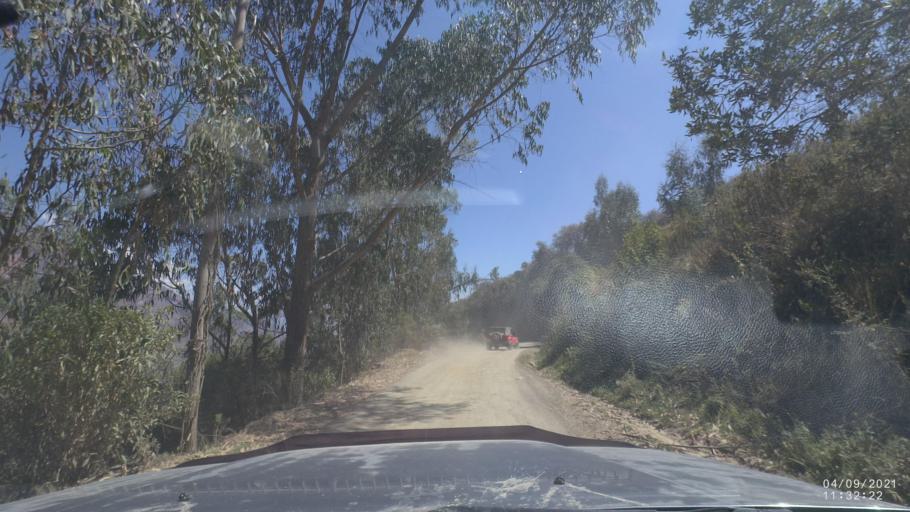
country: BO
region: Cochabamba
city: Colchani
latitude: -17.2297
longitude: -66.5215
